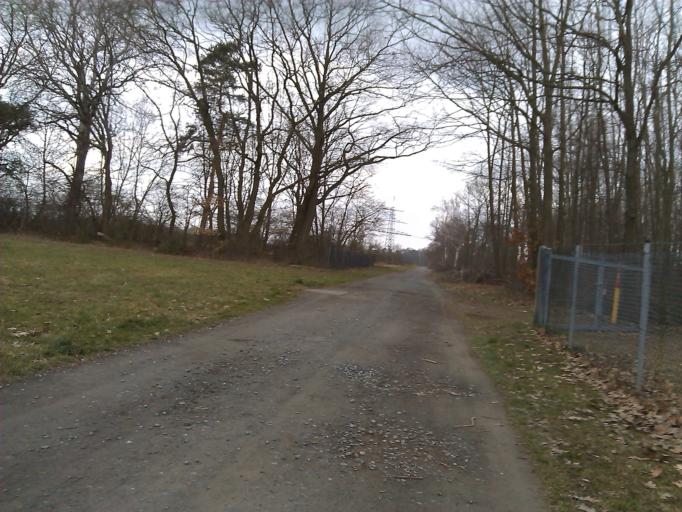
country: DE
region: Hesse
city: Pfungstadt
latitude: 49.8222
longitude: 8.5691
